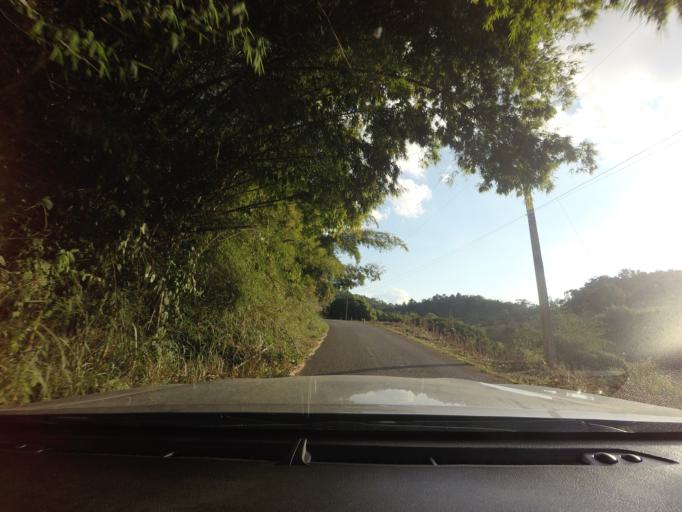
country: TH
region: Chiang Mai
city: Phrao
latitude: 19.5171
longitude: 99.1658
